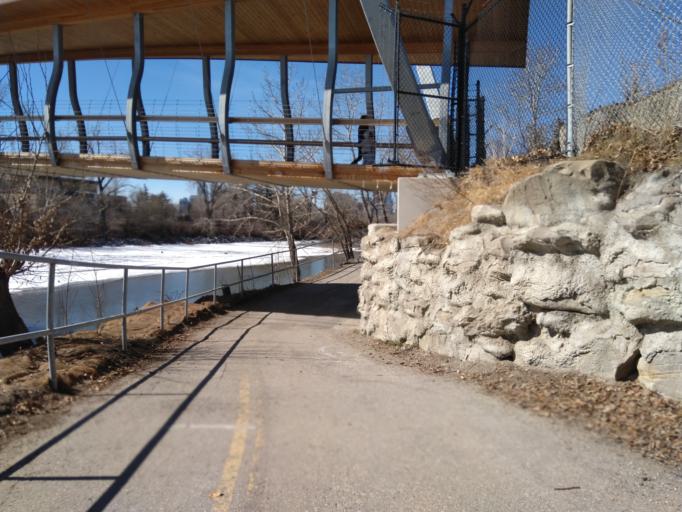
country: CA
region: Alberta
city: Calgary
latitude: 51.0468
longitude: -114.0306
